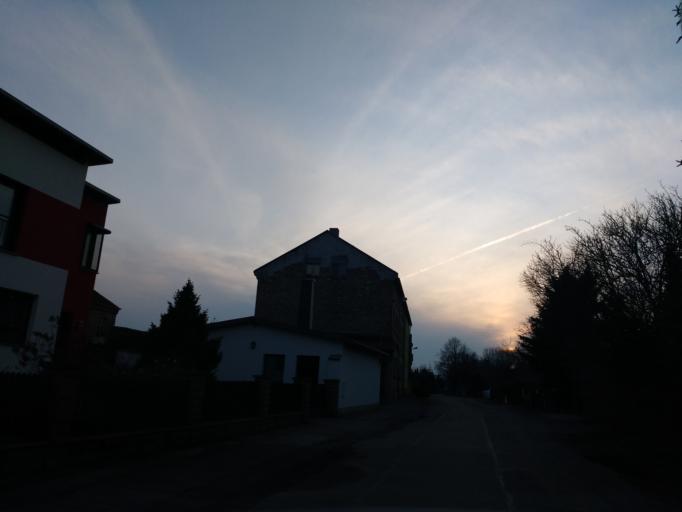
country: DE
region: Saxony-Anhalt
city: Halle (Saale)
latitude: 51.5290
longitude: 12.0063
